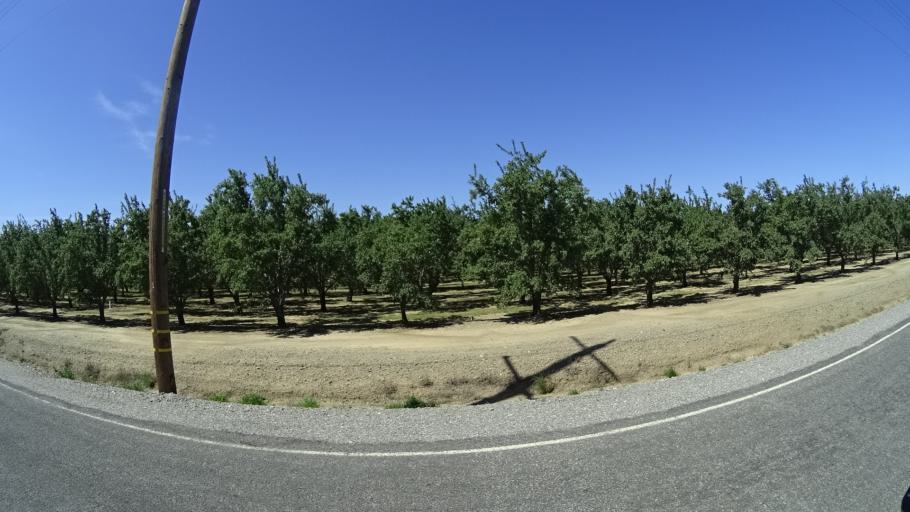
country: US
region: California
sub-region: Glenn County
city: Orland
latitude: 39.7082
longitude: -122.1784
